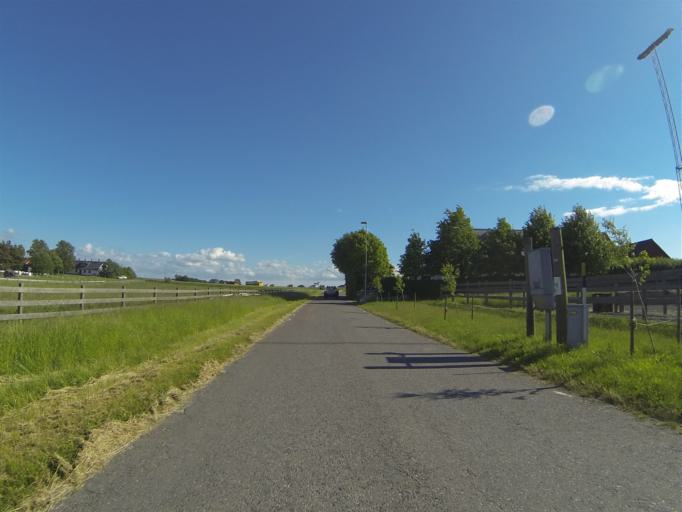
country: SE
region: Skane
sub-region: Staffanstorps Kommun
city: Staffanstorp
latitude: 55.6688
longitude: 13.2010
